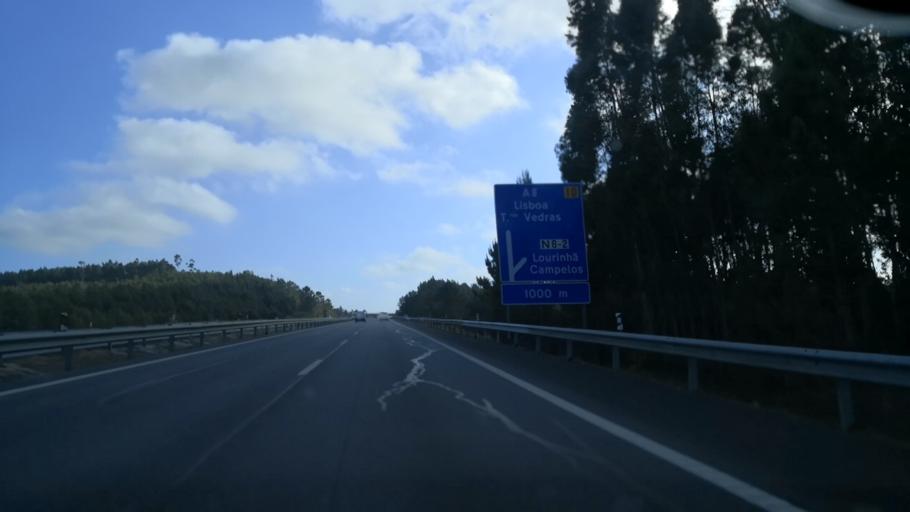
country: PT
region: Leiria
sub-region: Bombarral
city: Bombarral
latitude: 39.2030
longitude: -9.1920
